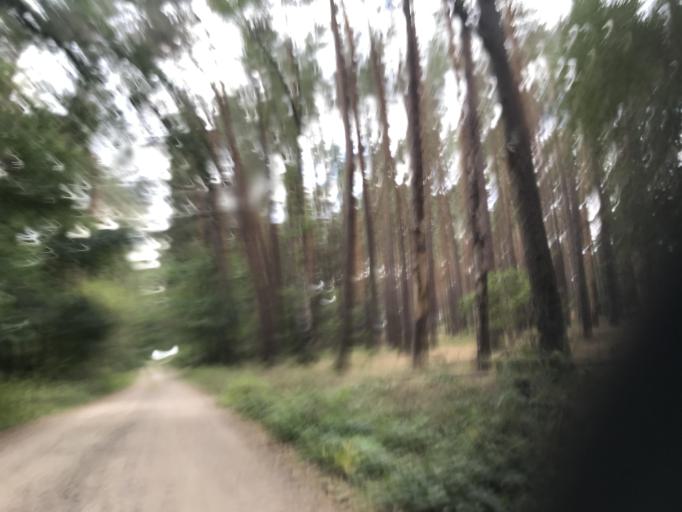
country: DE
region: Lower Saxony
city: Neetze
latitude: 53.2609
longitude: 10.6001
